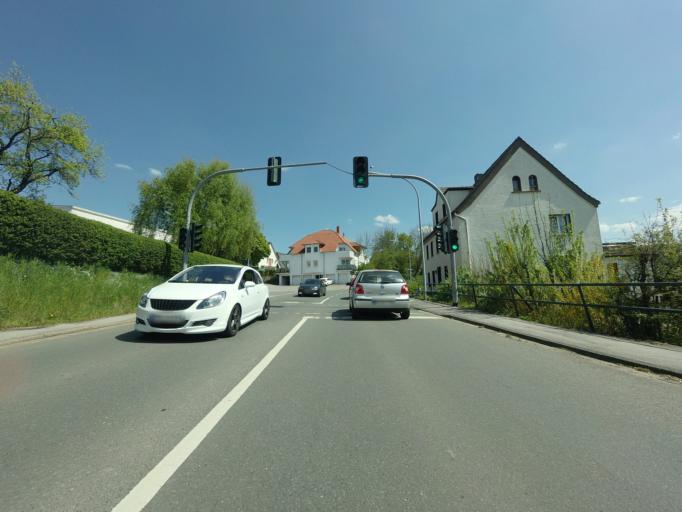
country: DE
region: North Rhine-Westphalia
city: Hemer
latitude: 51.3748
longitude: 7.7945
